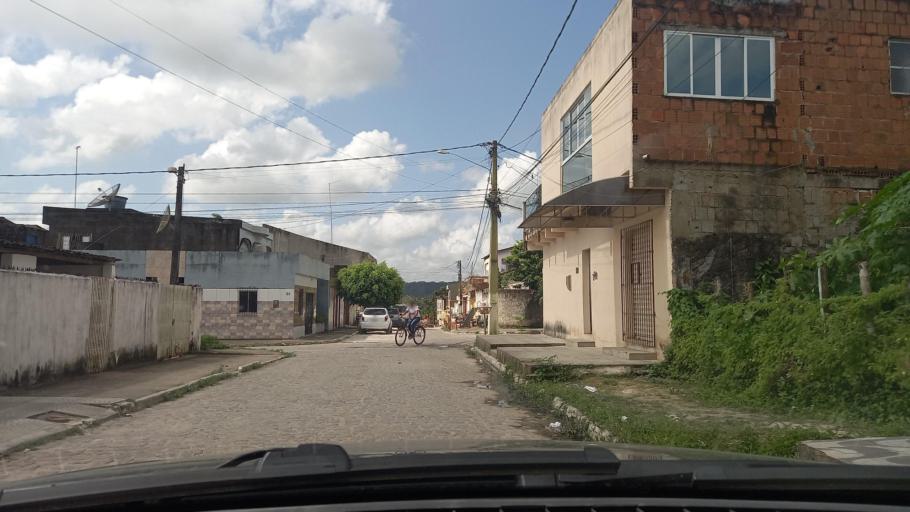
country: BR
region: Pernambuco
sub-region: Goiana
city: Goiana
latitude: -7.5591
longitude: -34.9942
